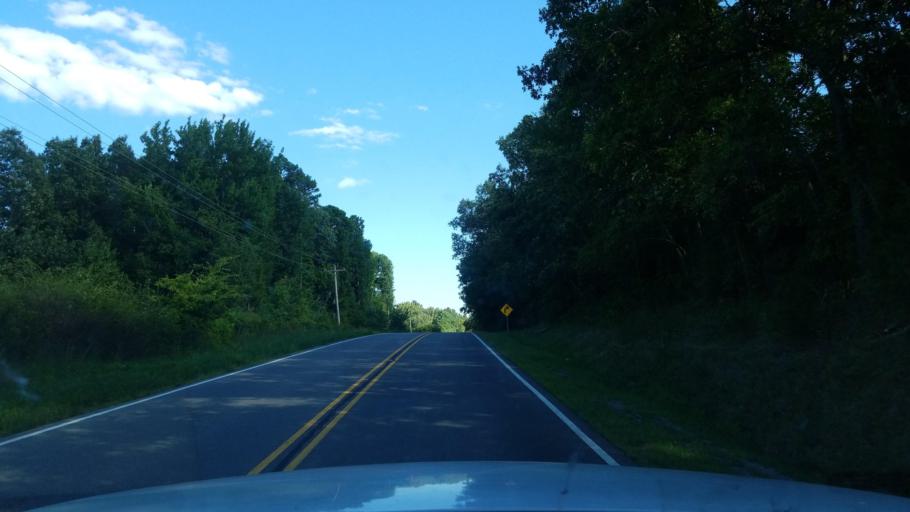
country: US
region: Illinois
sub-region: Saline County
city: Harrisburg
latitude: 37.6339
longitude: -88.4806
